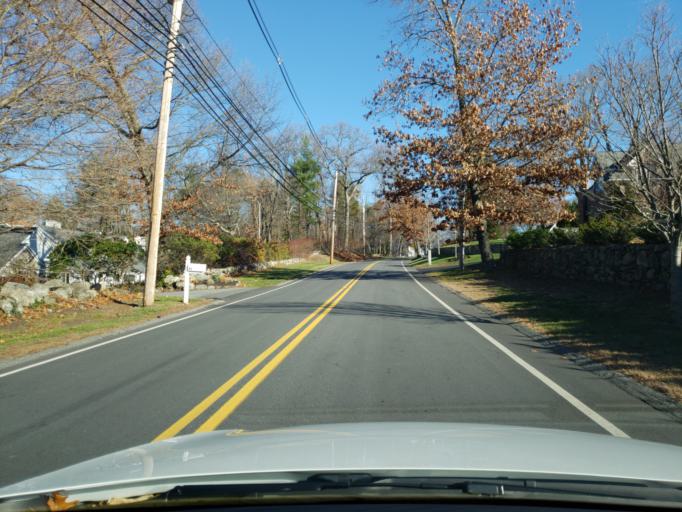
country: US
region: Massachusetts
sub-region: Essex County
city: Andover
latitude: 42.6377
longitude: -71.1399
